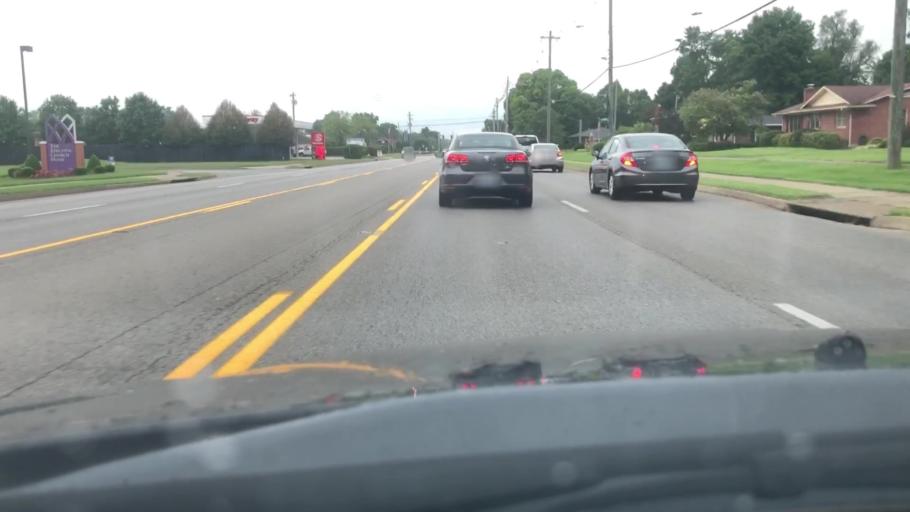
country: US
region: Kentucky
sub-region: Jefferson County
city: Graymoor-Devondale
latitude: 38.2721
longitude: -85.6126
